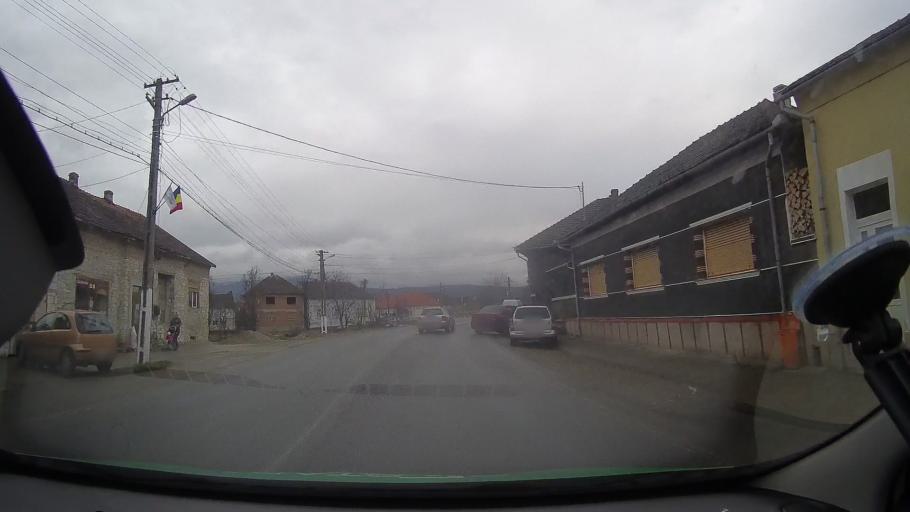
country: RO
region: Arad
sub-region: Comuna Buteni
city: Buteni
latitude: 46.3266
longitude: 22.1235
